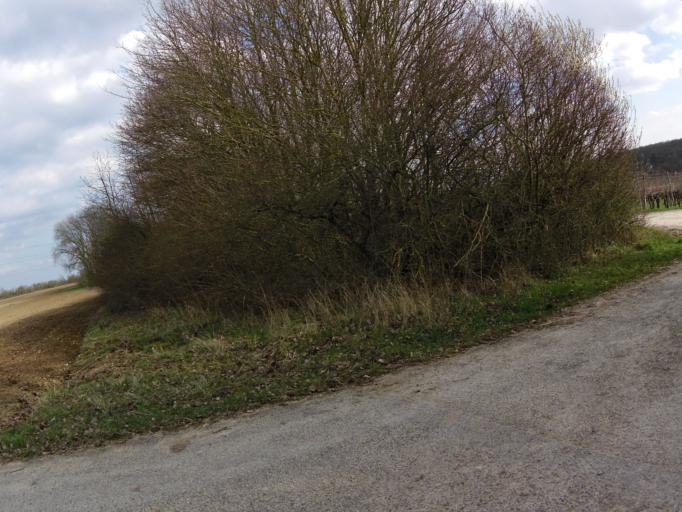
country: DE
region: Bavaria
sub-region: Regierungsbezirk Unterfranken
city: Buchbrunn
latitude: 49.7381
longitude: 10.1115
